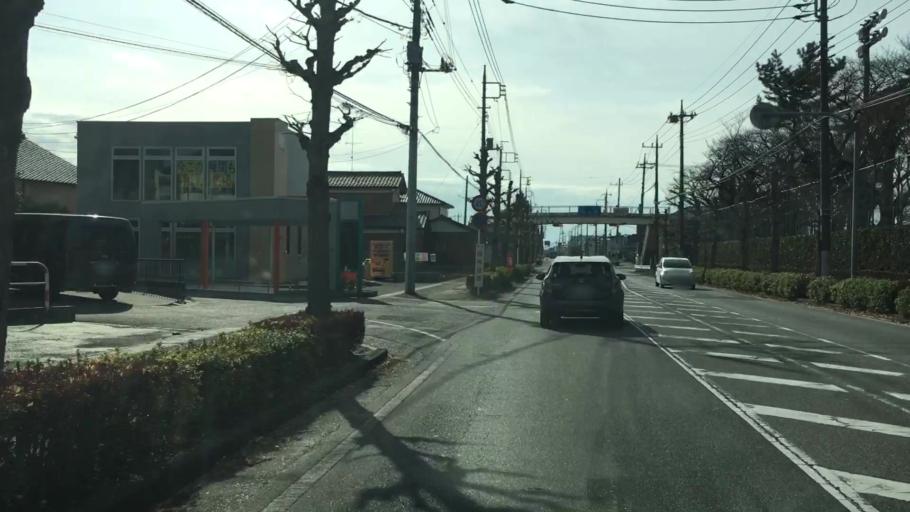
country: JP
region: Saitama
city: Menuma
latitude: 36.2447
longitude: 139.4091
